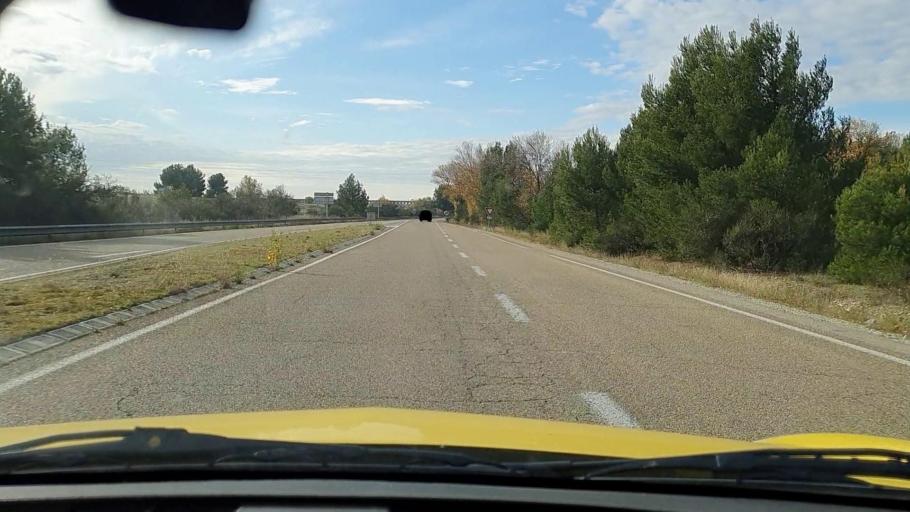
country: FR
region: Provence-Alpes-Cote d'Azur
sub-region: Departement du Vaucluse
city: Avignon
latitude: 43.9469
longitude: 4.7855
